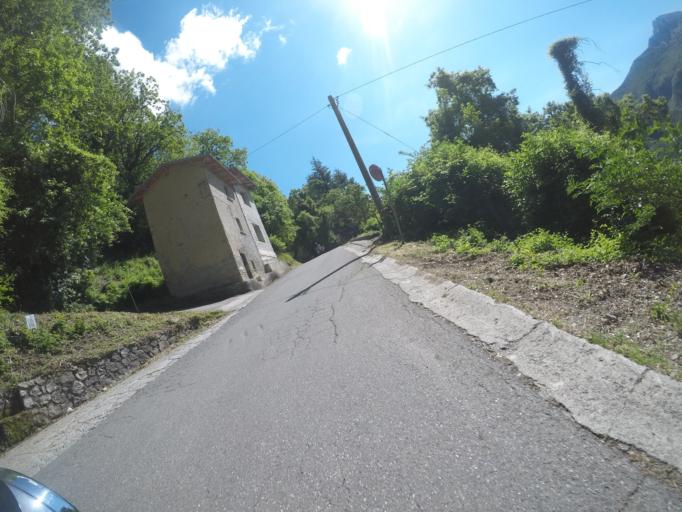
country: IT
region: Tuscany
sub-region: Provincia di Lucca
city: Careggine
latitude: 44.0702
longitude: 10.3172
